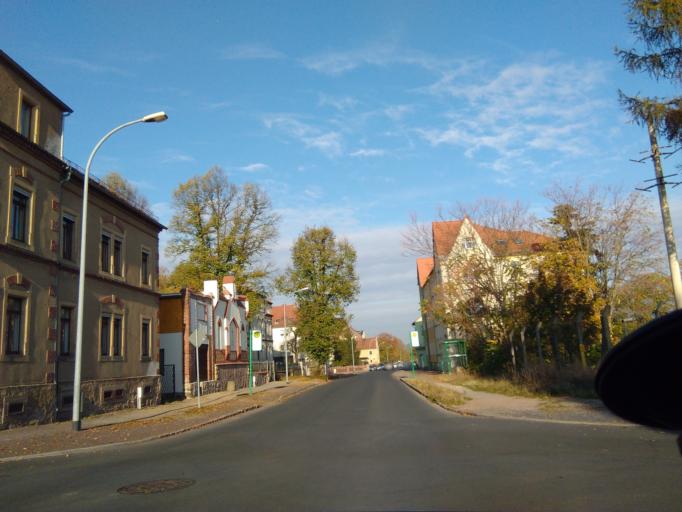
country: DE
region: Saxony
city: Meissen
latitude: 51.1562
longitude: 13.5075
